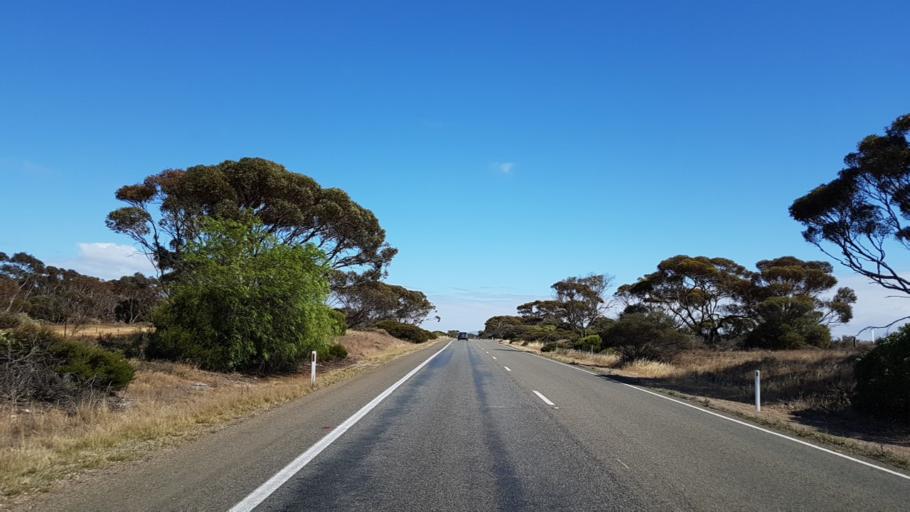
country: AU
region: South Australia
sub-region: Wakefield
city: Balaklava
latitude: -34.2495
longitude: 138.2186
